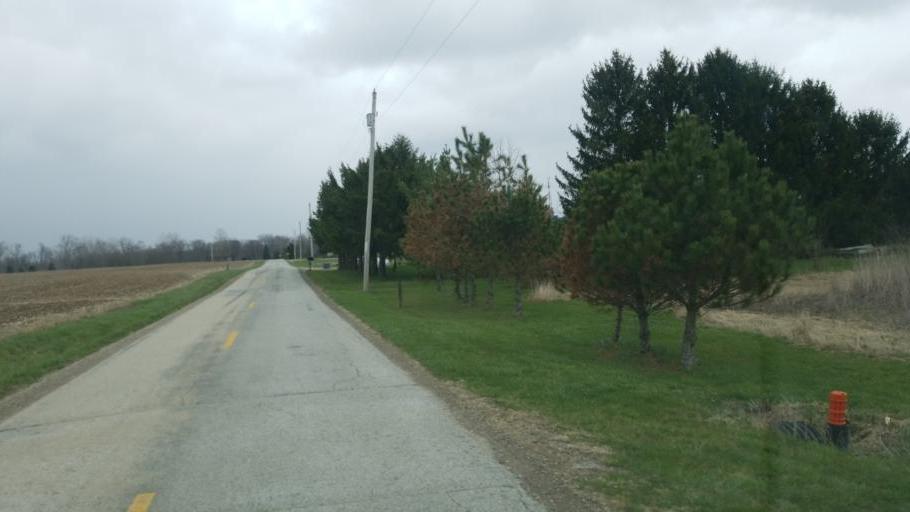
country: US
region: Ohio
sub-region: Marion County
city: Prospect
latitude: 40.4010
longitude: -83.2022
